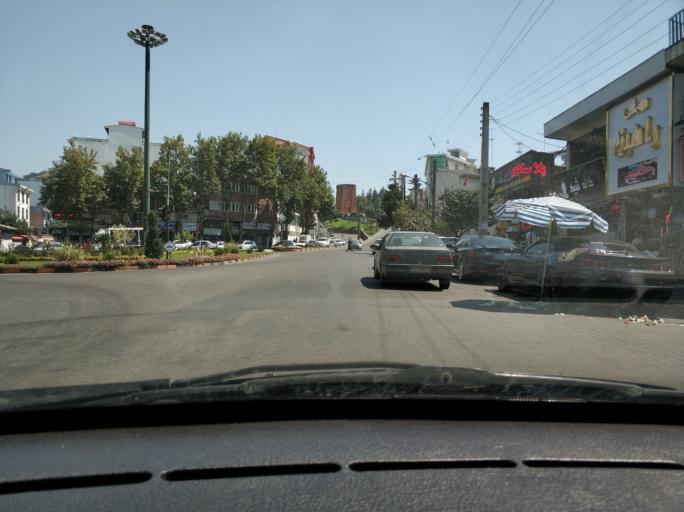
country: IR
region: Gilan
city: Lahijan
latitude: 37.1975
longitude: 50.0133
